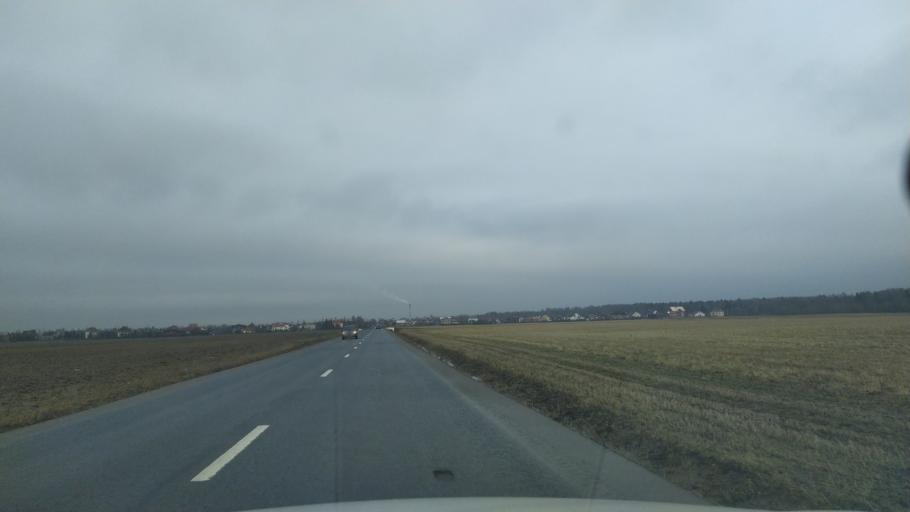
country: RU
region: St.-Petersburg
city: Aleksandrovskaya
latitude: 59.7168
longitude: 30.3381
